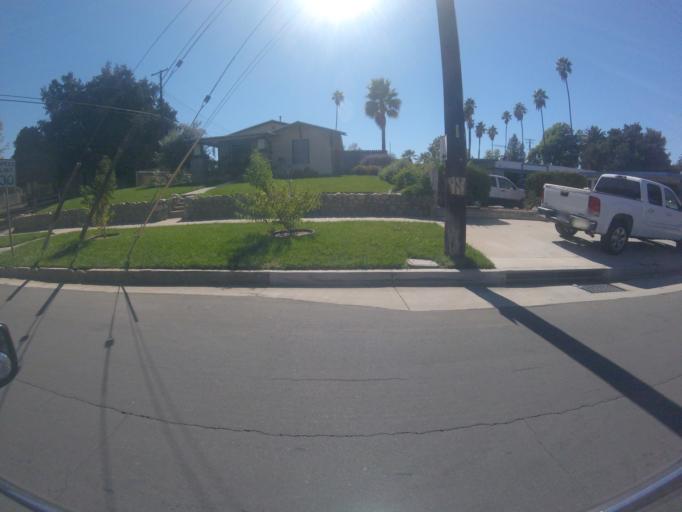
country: US
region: California
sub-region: San Bernardino County
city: Redlands
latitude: 34.0628
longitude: -117.1733
